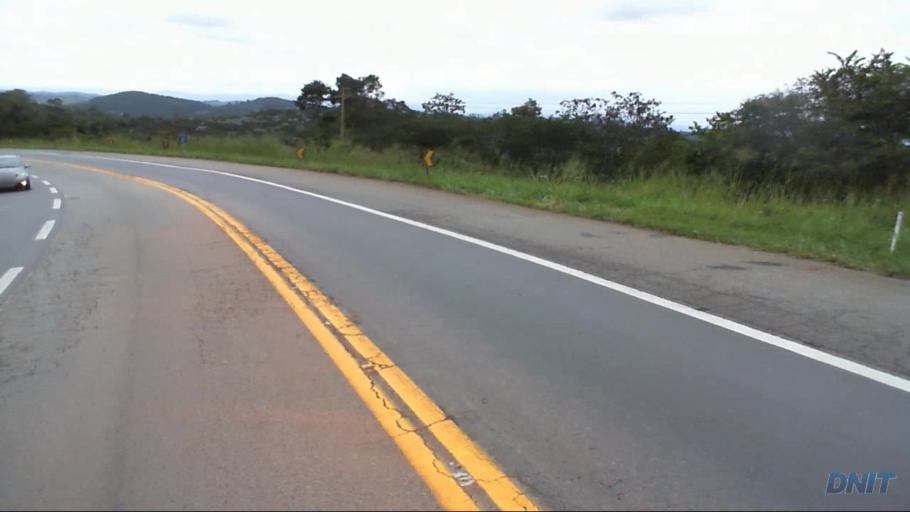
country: BR
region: Minas Gerais
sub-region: Barao De Cocais
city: Barao de Cocais
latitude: -19.7396
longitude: -43.5158
